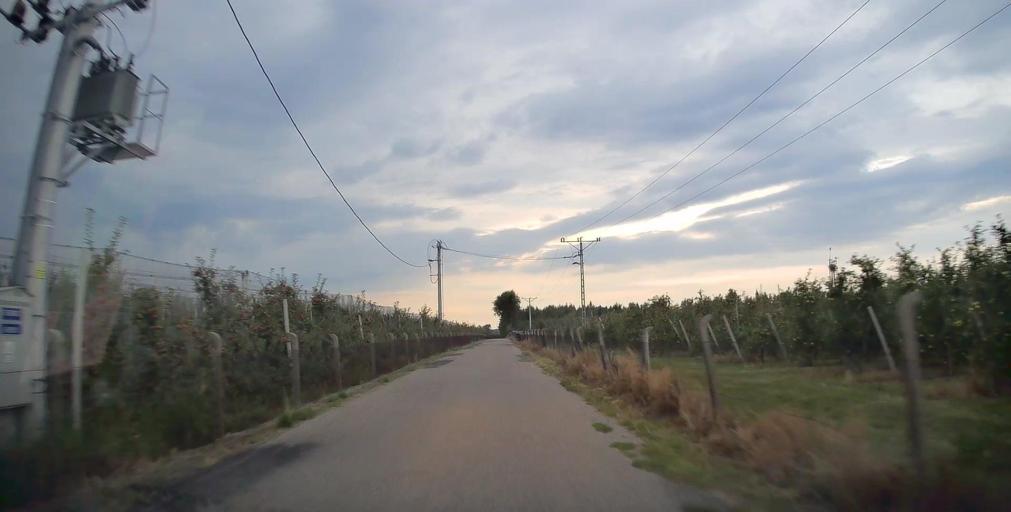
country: PL
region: Masovian Voivodeship
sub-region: Powiat grojecki
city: Jasieniec
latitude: 51.7921
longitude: 20.8966
